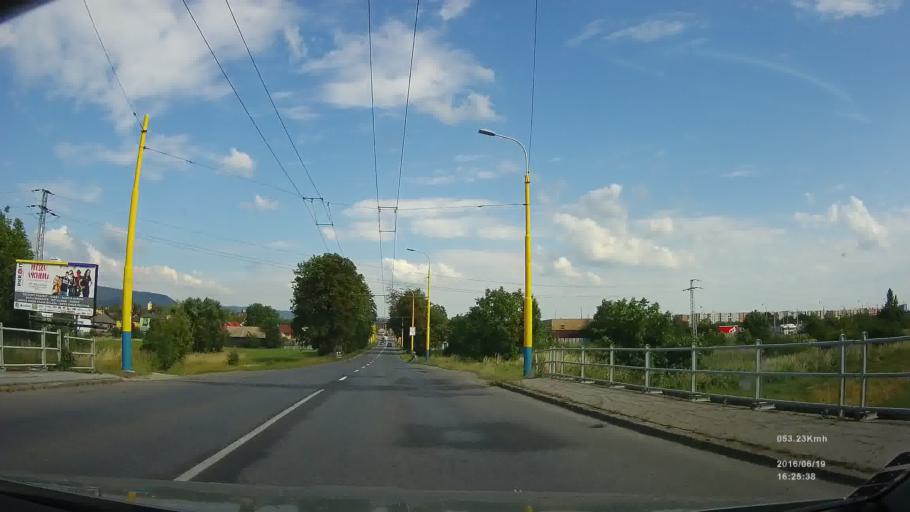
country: SK
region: Presovsky
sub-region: Okres Presov
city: Presov
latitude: 48.9808
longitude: 21.2578
